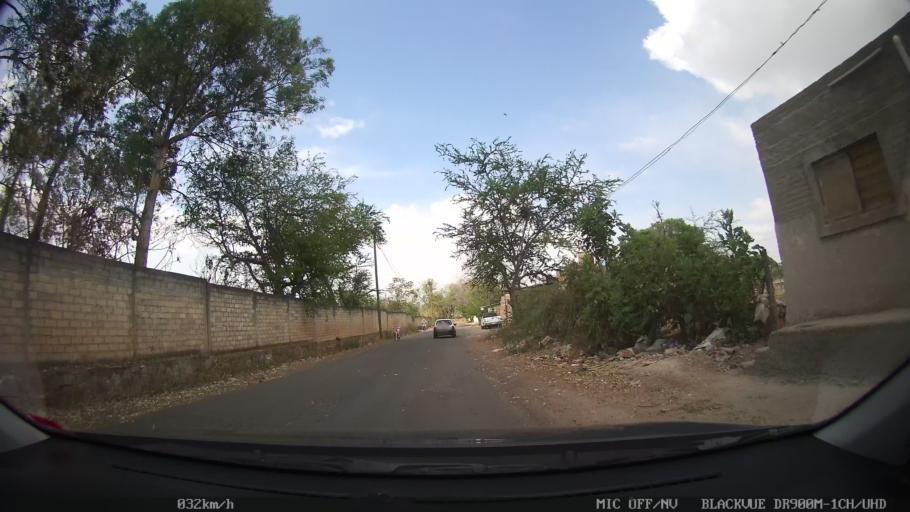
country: MX
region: Jalisco
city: Tonala
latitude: 20.6281
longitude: -103.2254
